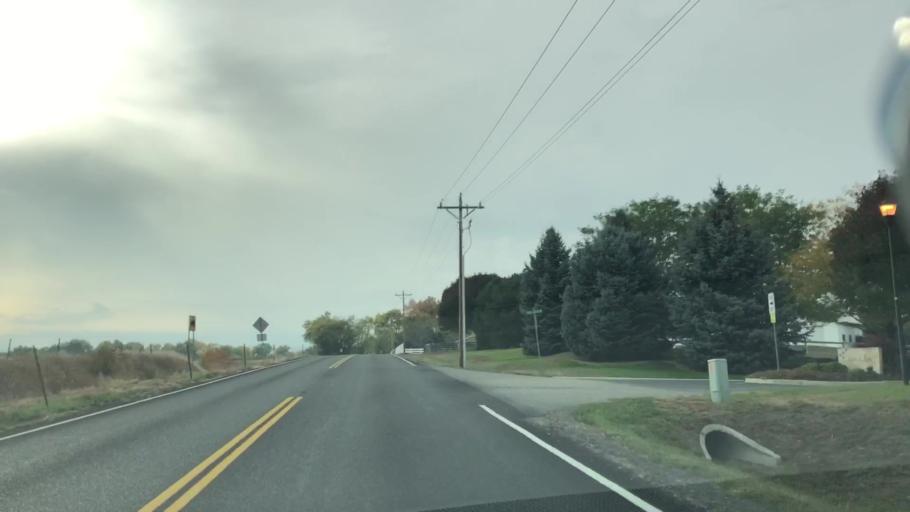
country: US
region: Colorado
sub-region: Larimer County
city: Loveland
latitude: 40.4656
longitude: -105.0501
